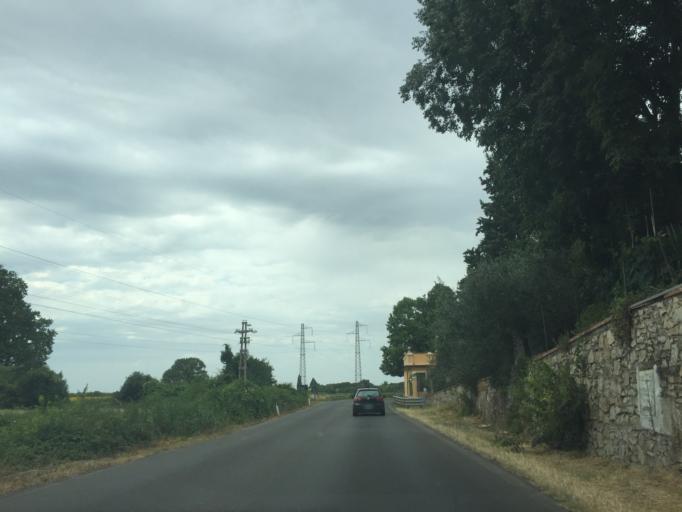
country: IT
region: Tuscany
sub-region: Province of Pisa
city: Gabella
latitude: 43.7268
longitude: 10.4889
